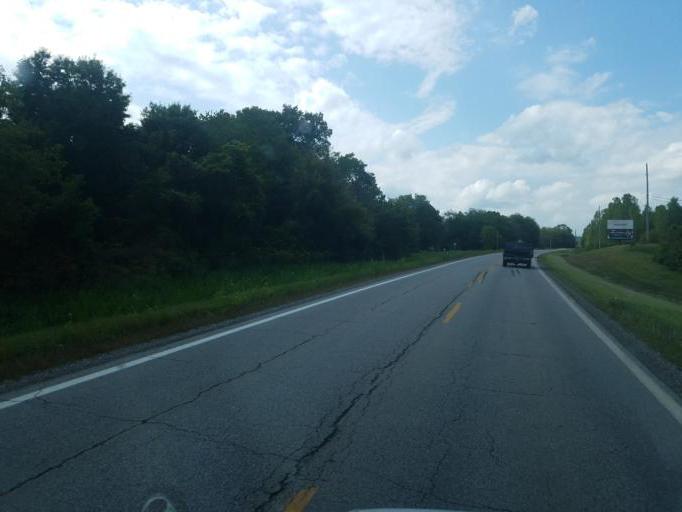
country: US
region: Ohio
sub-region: Sandusky County
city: Bellville
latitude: 40.6118
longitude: -82.4916
